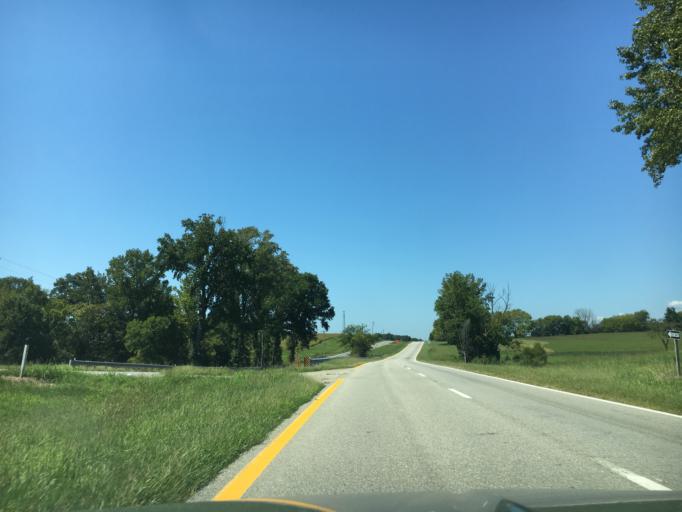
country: US
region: Virginia
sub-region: City of Danville
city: Danville
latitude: 36.5808
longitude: -79.1783
